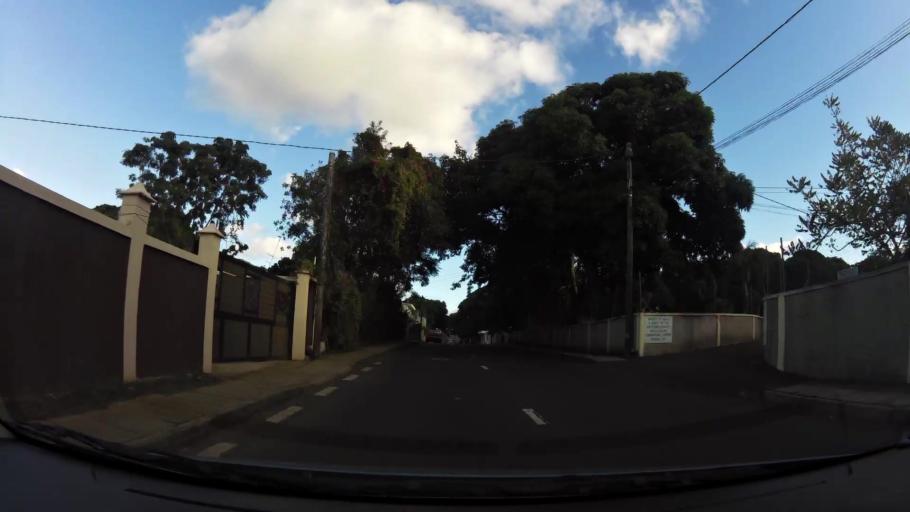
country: MU
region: Plaines Wilhems
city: Ebene
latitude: -20.2275
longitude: 57.4635
